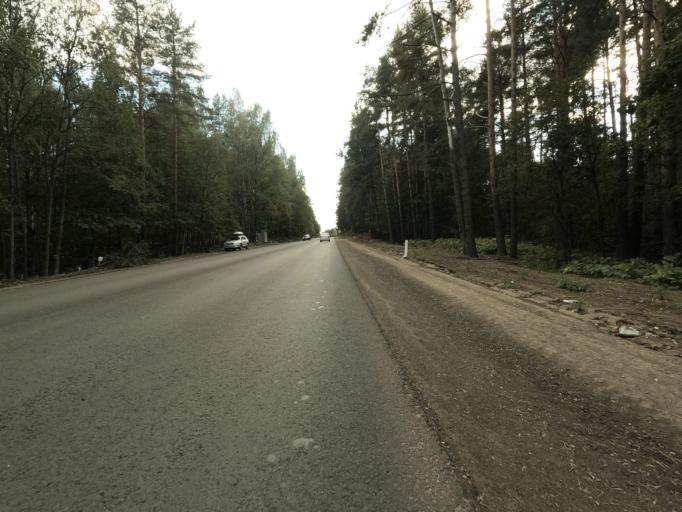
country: RU
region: Leningrad
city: Koltushi
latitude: 59.9572
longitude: 30.6588
